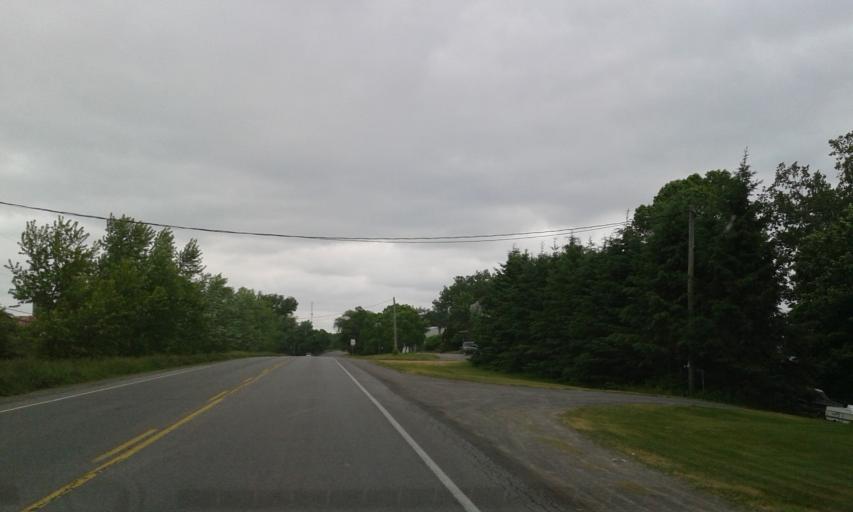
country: CA
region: Ontario
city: Prince Edward
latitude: 43.9563
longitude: -77.3257
